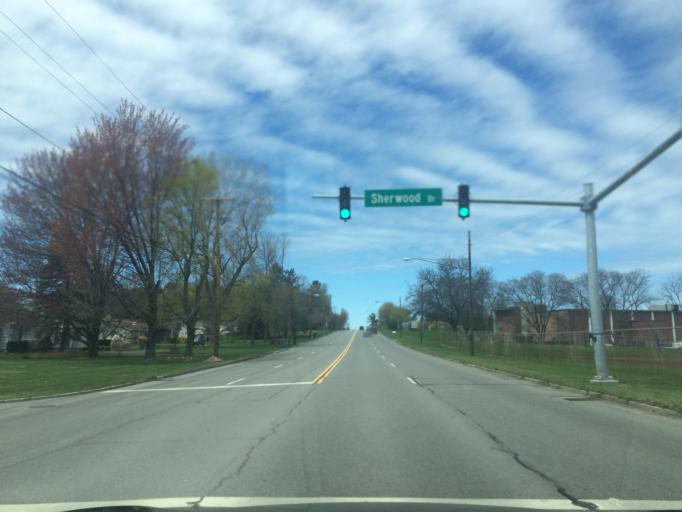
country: US
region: New York
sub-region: Monroe County
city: East Rochester
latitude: 43.1066
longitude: -77.4943
